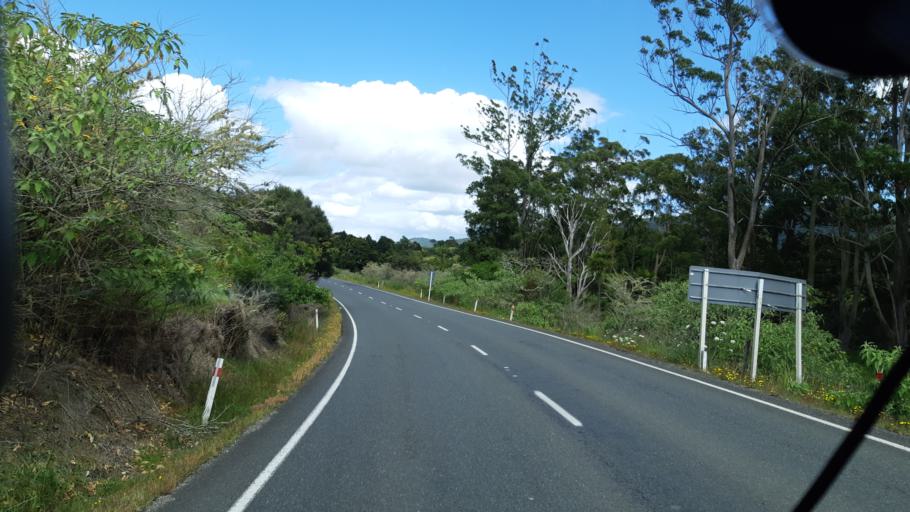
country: NZ
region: Northland
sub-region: Far North District
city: Waimate North
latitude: -35.2882
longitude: 173.7163
